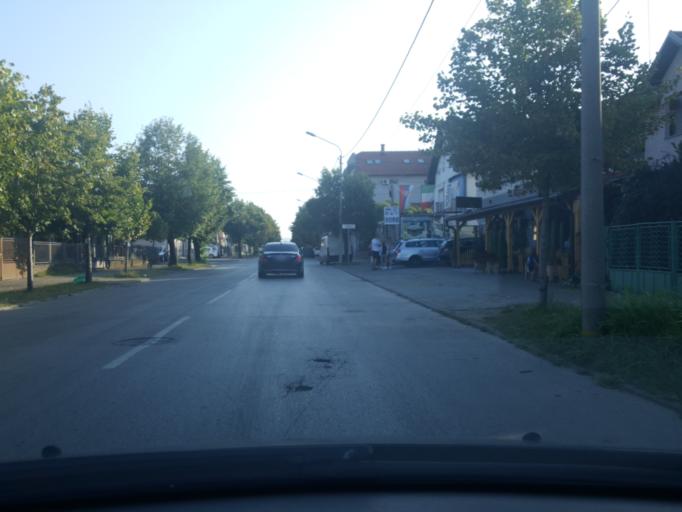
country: RS
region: Central Serbia
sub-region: Macvanski Okrug
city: Sabac
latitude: 44.7453
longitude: 19.6995
